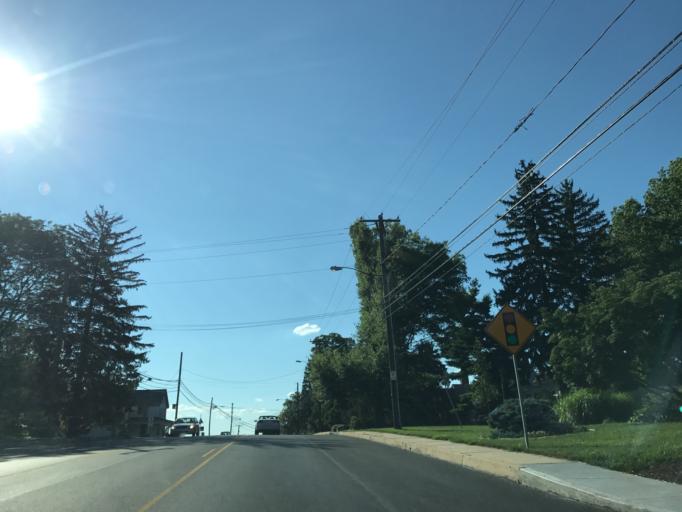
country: US
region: Pennsylvania
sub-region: Lancaster County
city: Elizabethtown
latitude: 40.1414
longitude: -76.5925
